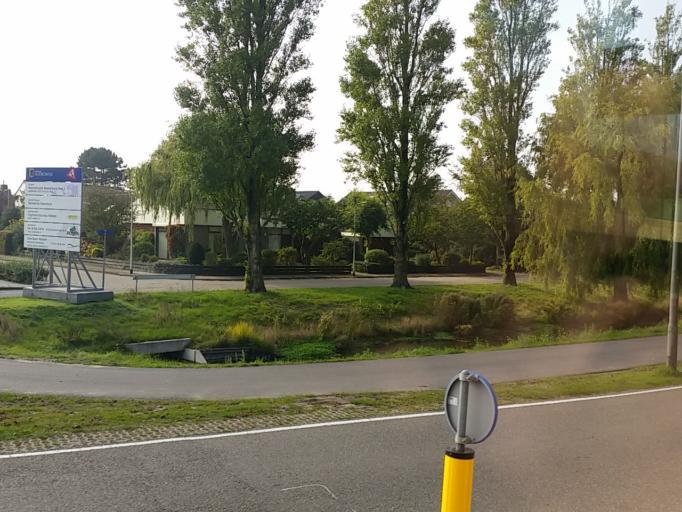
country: NL
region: South Holland
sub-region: Gemeente Noordwijk
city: Noordwijk-Binnen
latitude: 52.2416
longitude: 4.4603
